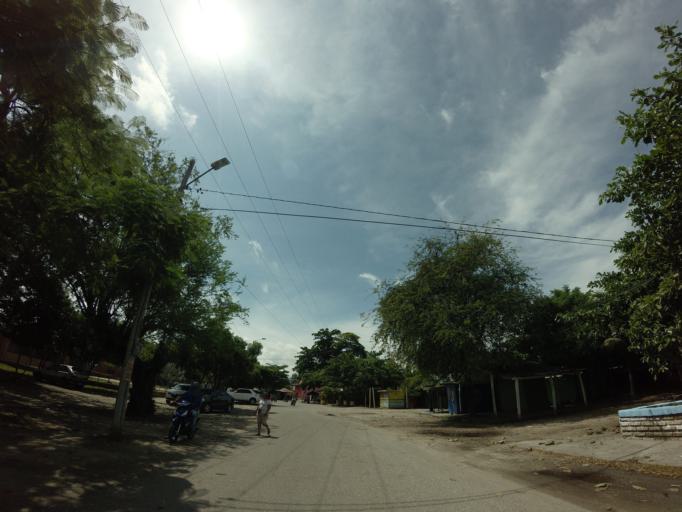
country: CO
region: Cundinamarca
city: Puerto Salgar
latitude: 5.4789
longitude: -74.6761
